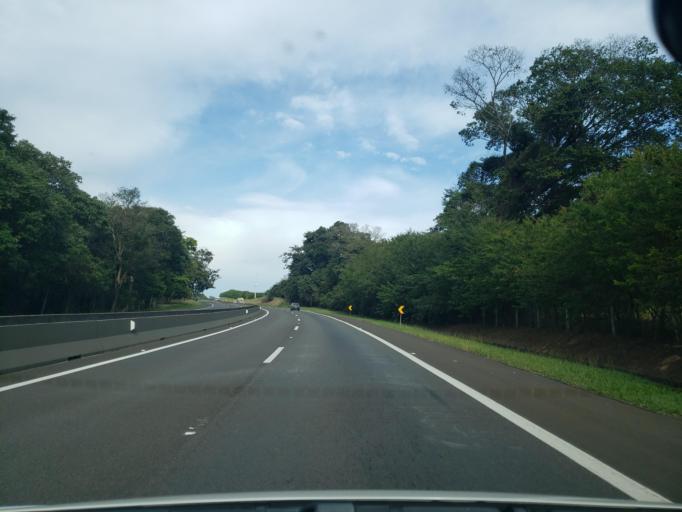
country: BR
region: Sao Paulo
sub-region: Brotas
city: Brotas
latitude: -22.2782
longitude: -47.9859
